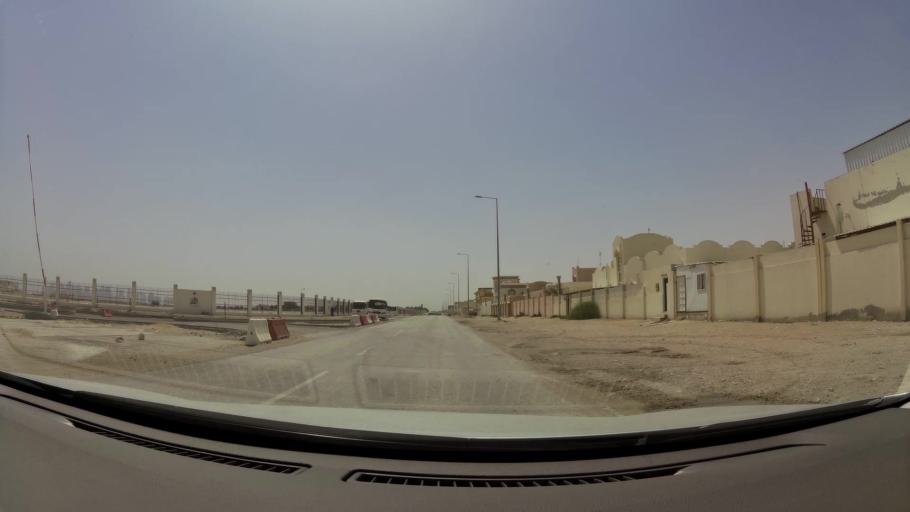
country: QA
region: Baladiyat Umm Salal
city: Umm Salal Muhammad
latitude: 25.3704
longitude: 51.4790
